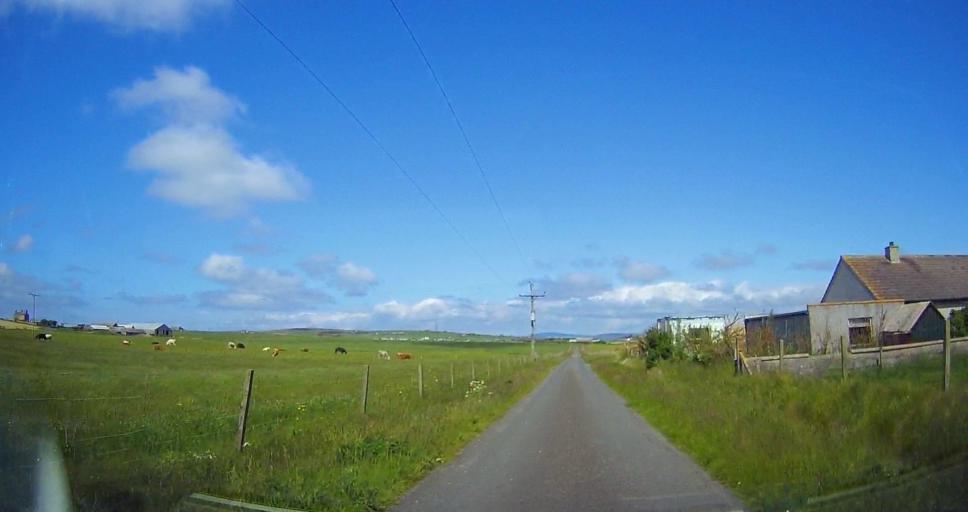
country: GB
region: Scotland
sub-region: Orkney Islands
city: Kirkwall
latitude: 58.8313
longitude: -2.8983
